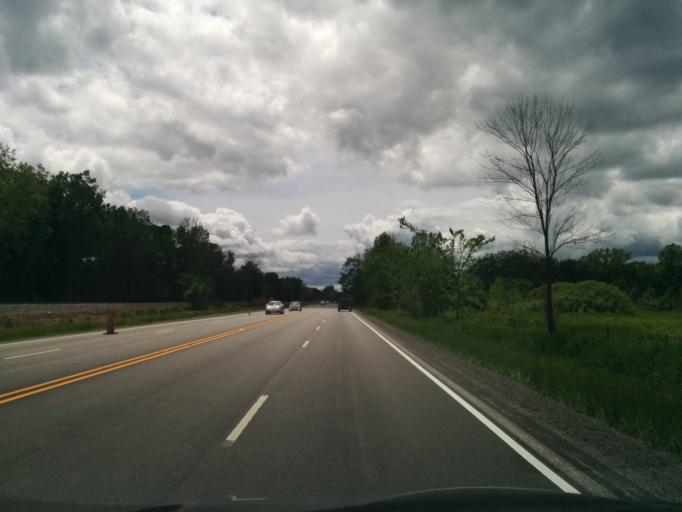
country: US
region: Indiana
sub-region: Porter County
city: Chesterton
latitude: 41.6418
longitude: -87.0258
